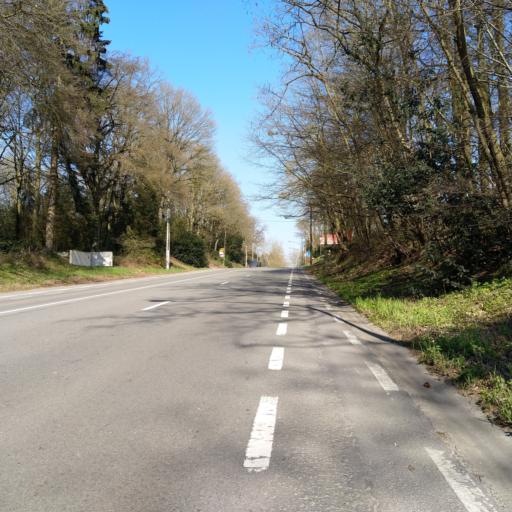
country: BE
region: Wallonia
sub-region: Province du Hainaut
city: Jurbise
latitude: 50.4978
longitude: 3.9359
